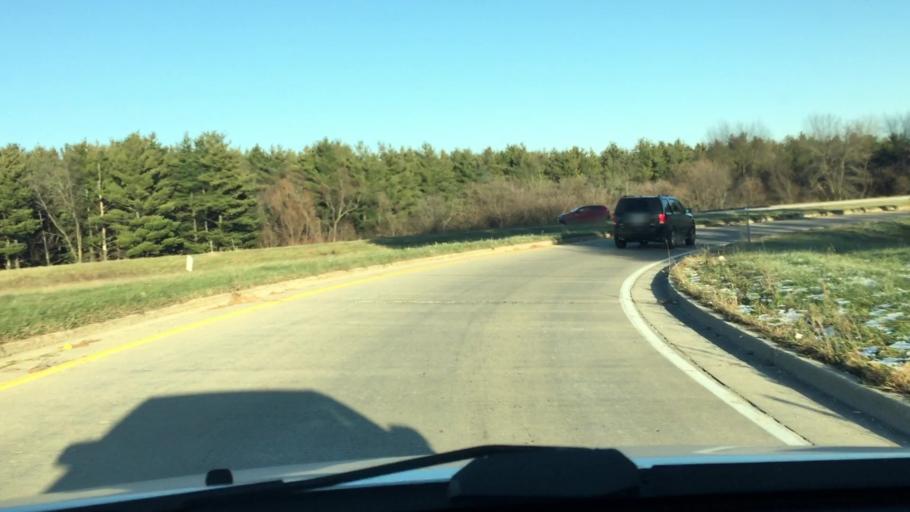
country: US
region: Wisconsin
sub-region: Waukesha County
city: Oconomowoc
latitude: 43.1094
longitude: -88.4787
